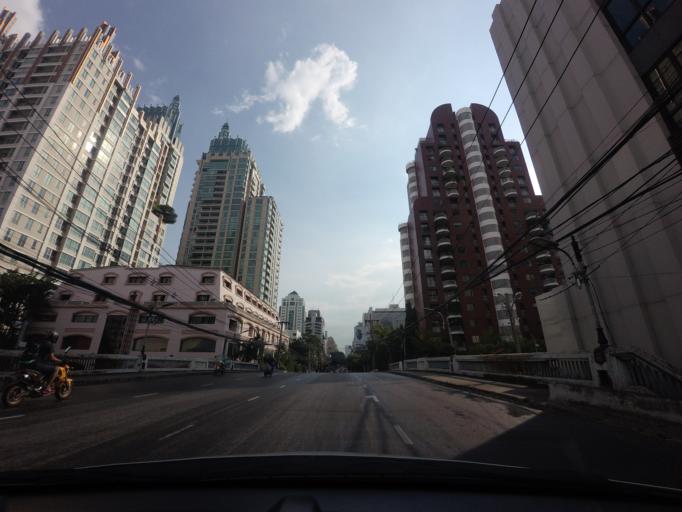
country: TH
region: Bangkok
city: Ratchathewi
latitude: 13.7488
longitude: 100.5447
